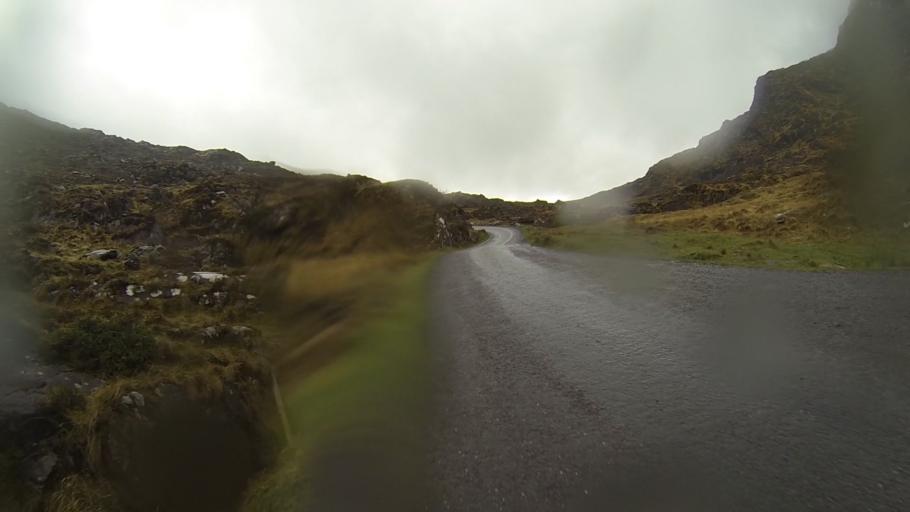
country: IE
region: Munster
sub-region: Ciarrai
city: Kenmare
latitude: 51.9977
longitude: -9.6439
